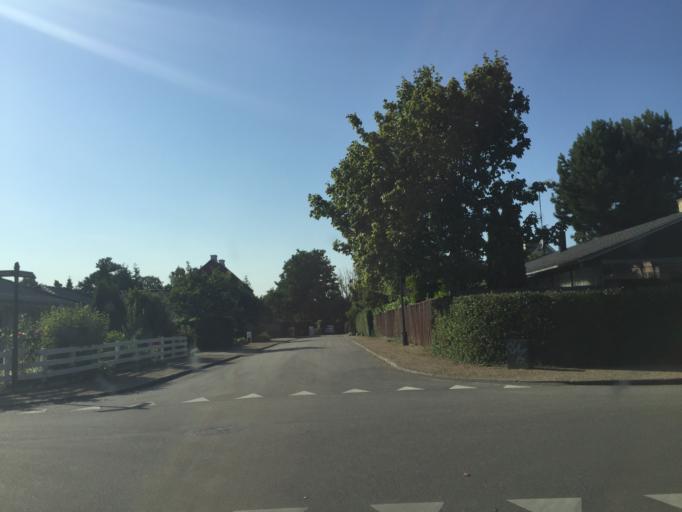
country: DK
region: Capital Region
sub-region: Gentofte Kommune
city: Charlottenlund
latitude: 55.7506
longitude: 12.5678
